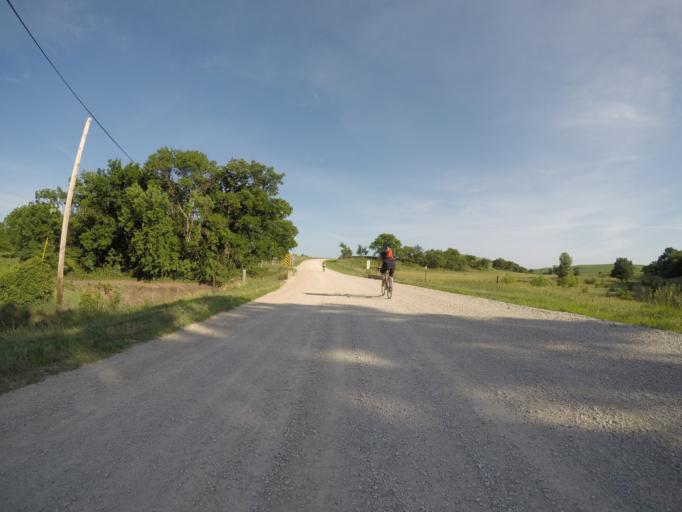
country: US
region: Kansas
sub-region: Riley County
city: Manhattan
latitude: 39.0583
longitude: -96.4979
